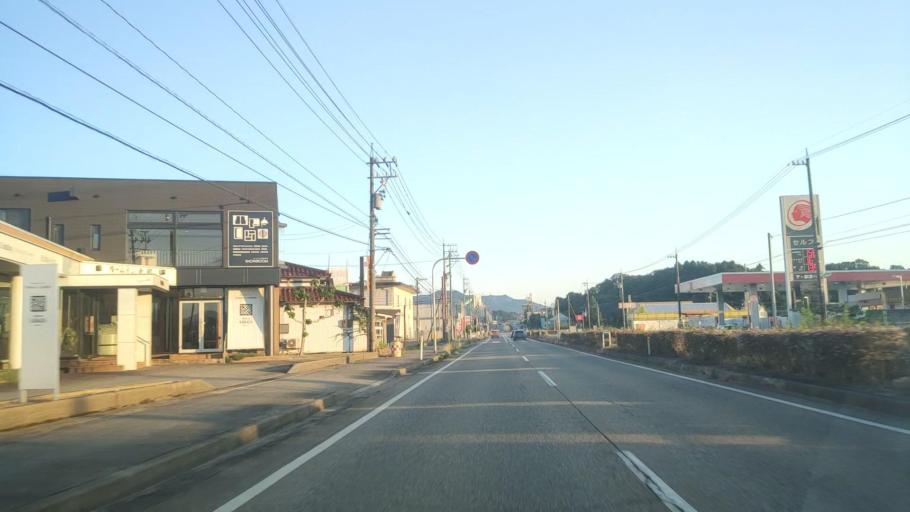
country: JP
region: Toyama
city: Himi
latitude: 36.8340
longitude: 136.9908
